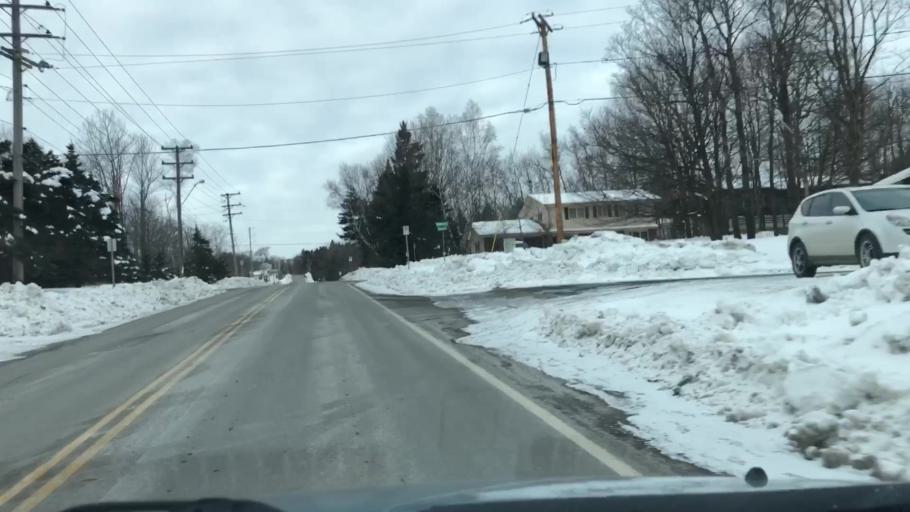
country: US
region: Minnesota
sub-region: Saint Louis County
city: Arnold
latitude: 46.8367
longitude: -92.0564
